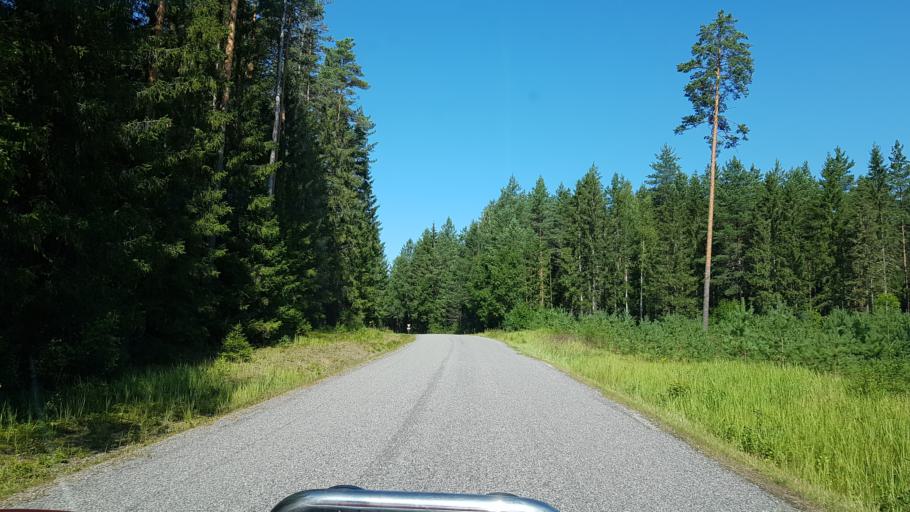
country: EE
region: Vorumaa
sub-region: Voru linn
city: Voru
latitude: 57.7326
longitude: 27.2079
